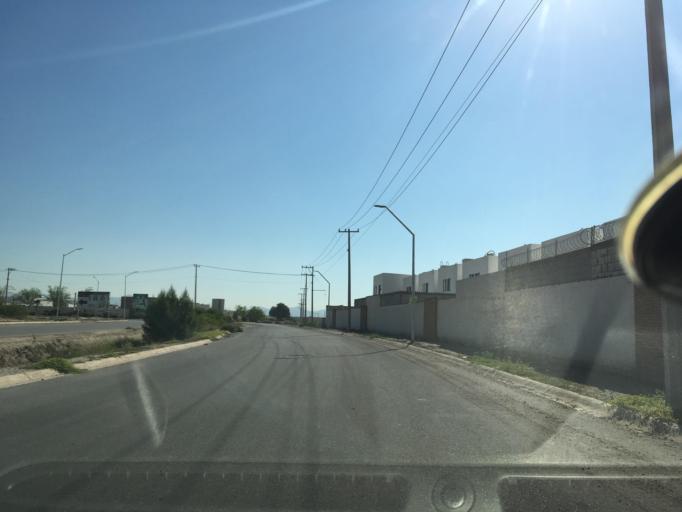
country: MX
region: Coahuila
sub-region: Torreon
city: Fraccionamiento la Noria
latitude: 25.5709
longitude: -103.3612
